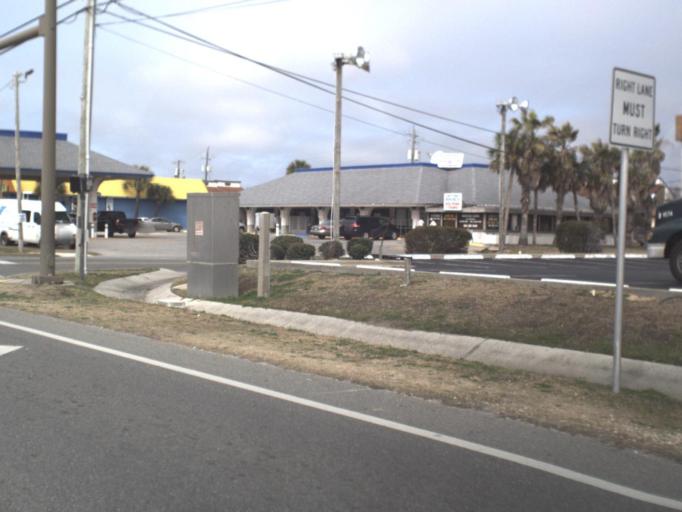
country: US
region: Florida
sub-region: Bay County
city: Panama City Beach
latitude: 30.1847
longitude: -85.8185
